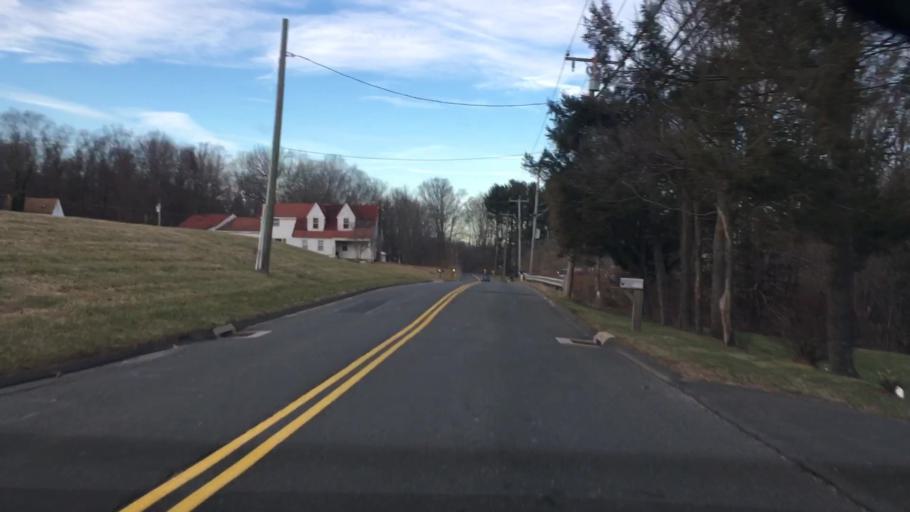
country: US
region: Connecticut
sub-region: New Haven County
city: Cheshire Village
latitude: 41.5429
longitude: -72.9279
